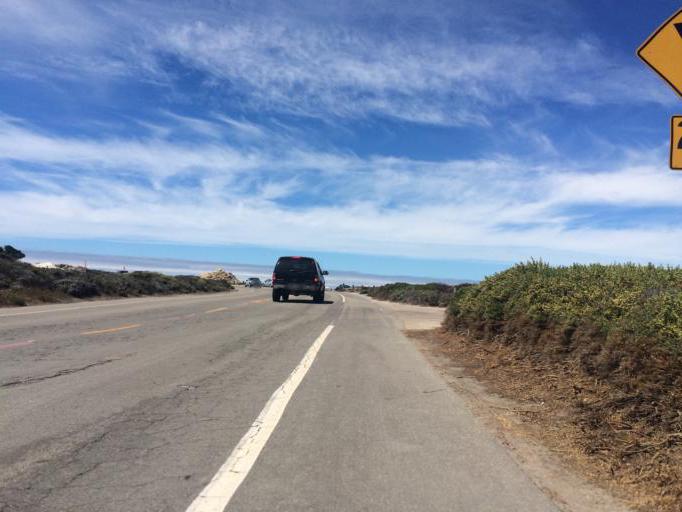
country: US
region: California
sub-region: Monterey County
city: Del Monte Forest
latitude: 36.6093
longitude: -121.9552
